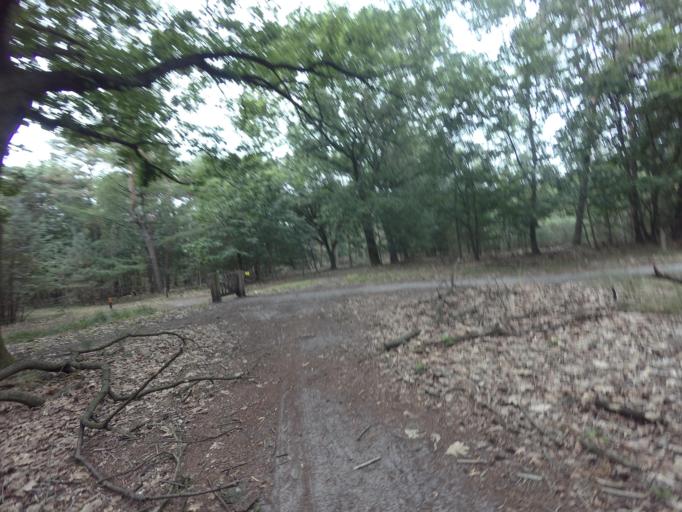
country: NL
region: North Brabant
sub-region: Gemeente Landerd
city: Schaijk
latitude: 51.7149
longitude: 5.6237
